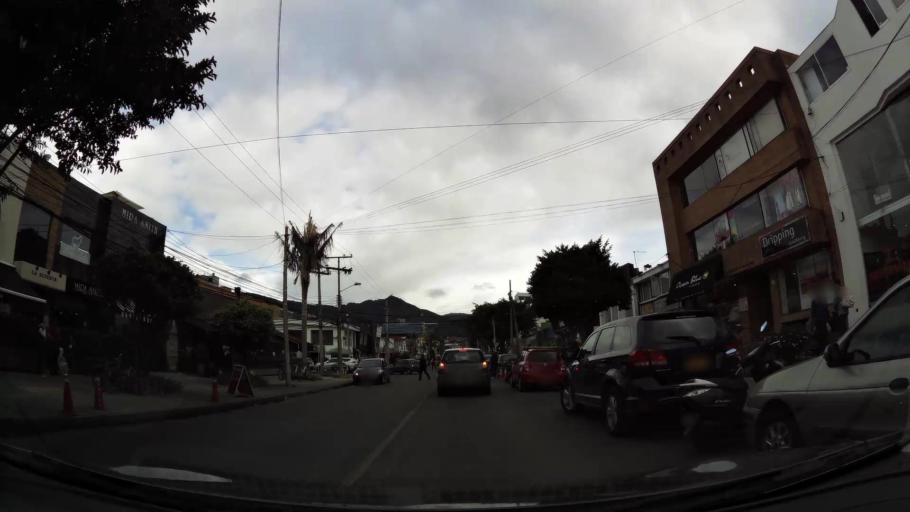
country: CO
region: Bogota D.C.
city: Barrio San Luis
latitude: 4.6938
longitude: -74.0475
